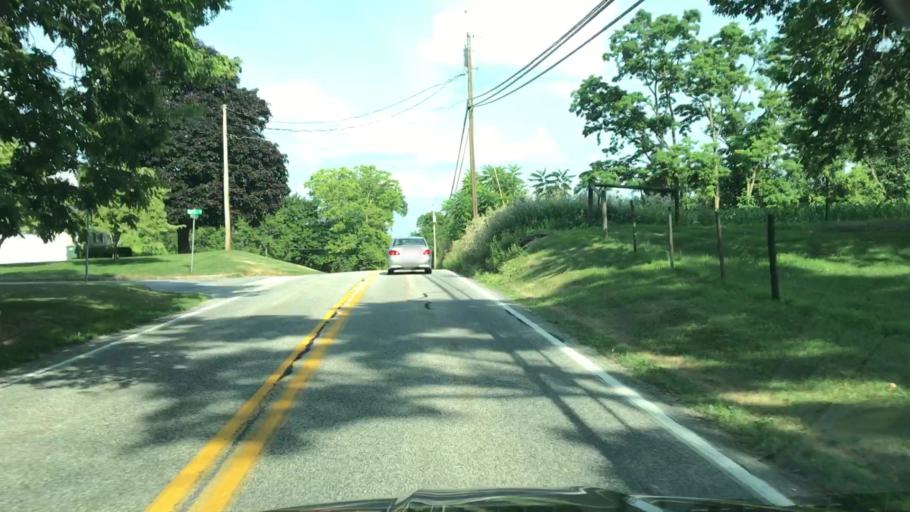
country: US
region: Pennsylvania
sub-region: Cumberland County
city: Boiling Springs
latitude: 40.1763
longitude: -77.0748
